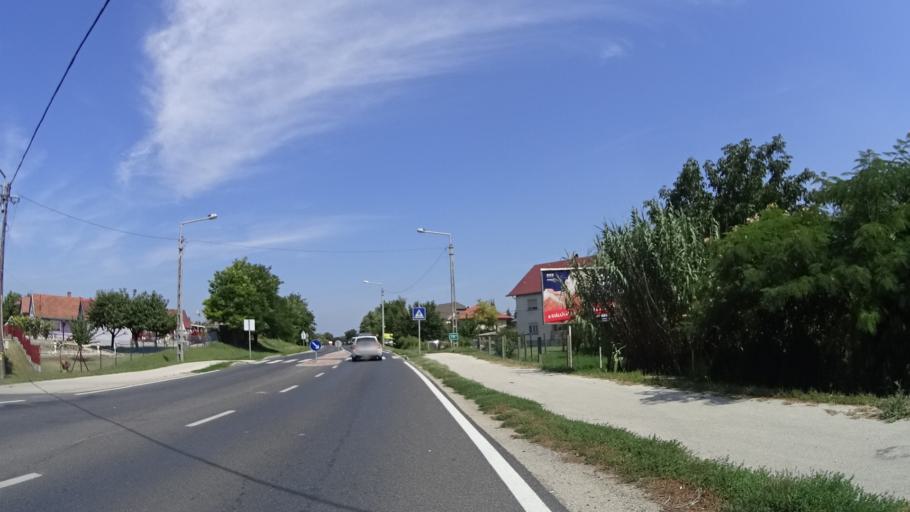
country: HU
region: Fejer
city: Szabadbattyan
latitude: 47.1239
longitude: 18.3763
